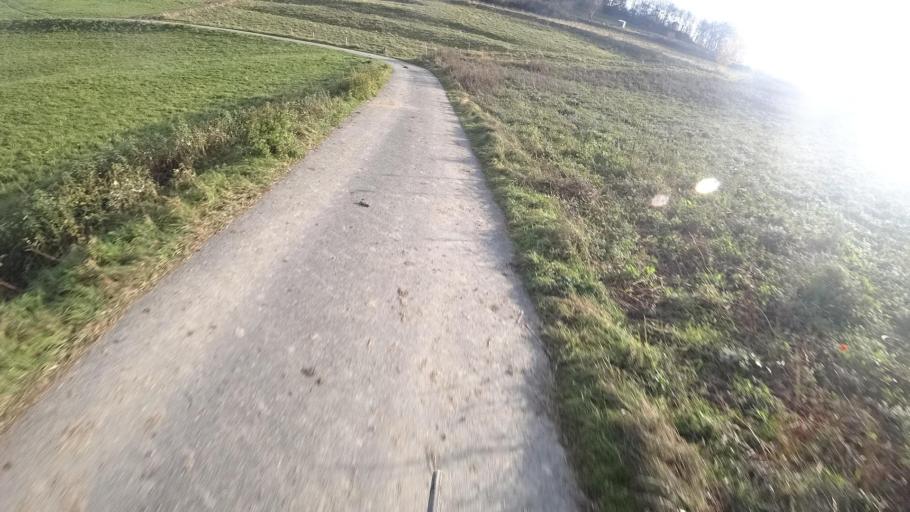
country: DE
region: Rheinland-Pfalz
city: Utzenhain
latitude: 50.1298
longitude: 7.6283
